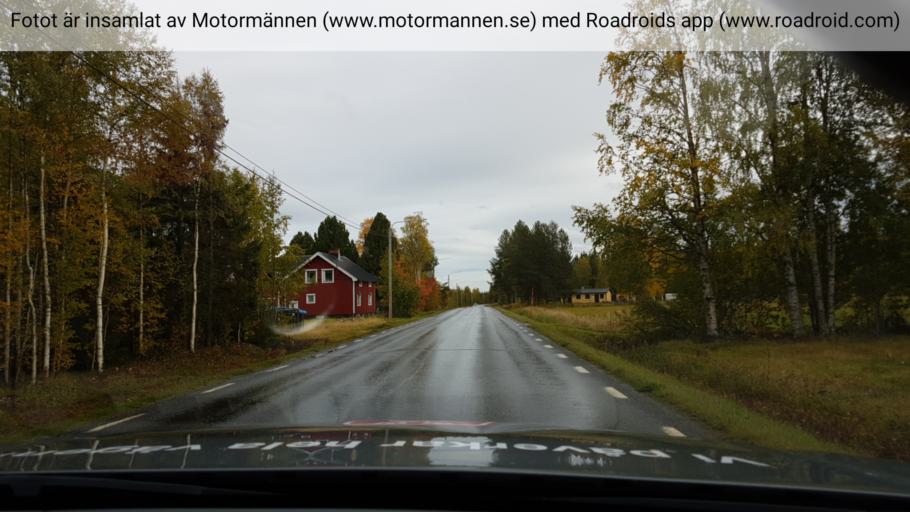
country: SE
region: Vaesterbotten
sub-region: Vilhelmina Kommun
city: Sjoberg
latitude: 64.6490
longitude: 16.3385
